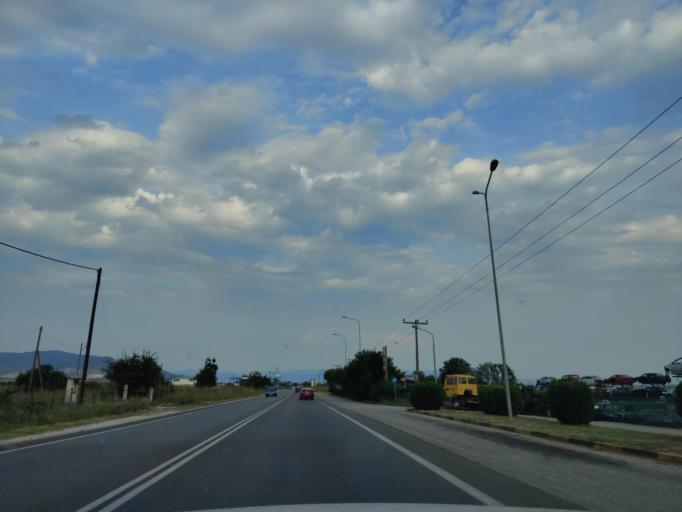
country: GR
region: East Macedonia and Thrace
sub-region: Nomos Dramas
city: Xiropotamos
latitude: 41.1605
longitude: 24.0858
